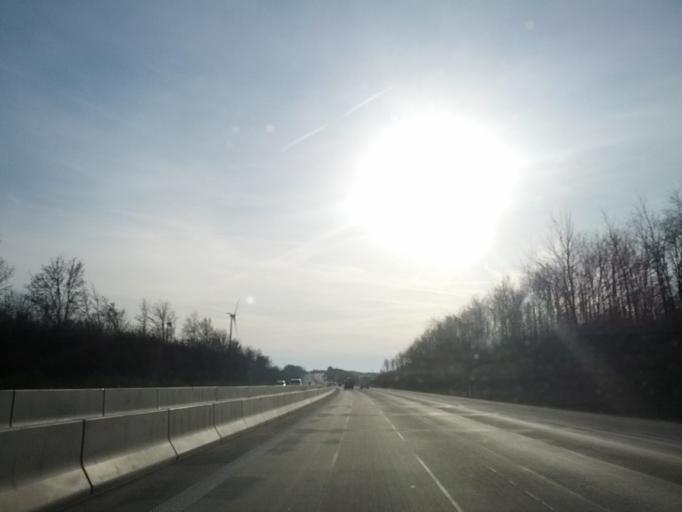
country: DE
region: Bavaria
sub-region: Regierungsbezirk Unterfranken
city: Martinsheim
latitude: 49.6114
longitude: 10.1721
